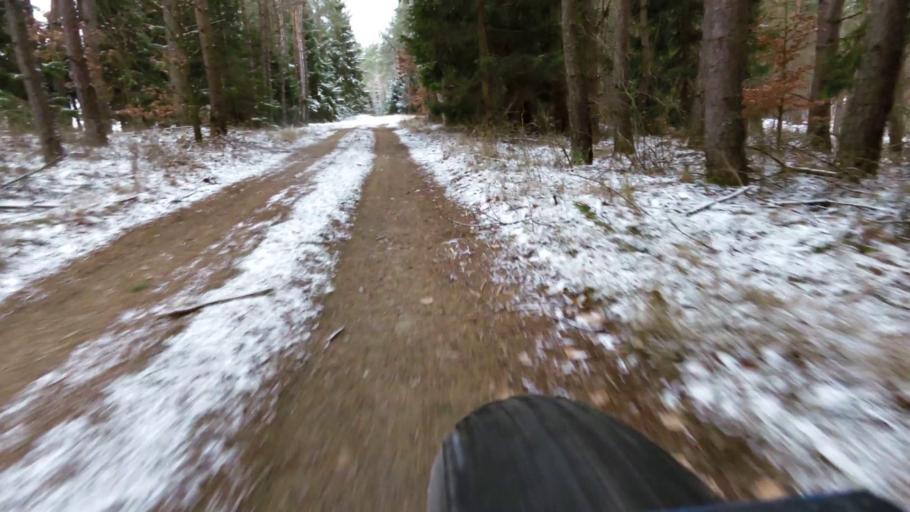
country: PL
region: West Pomeranian Voivodeship
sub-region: Powiat walecki
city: Miroslawiec
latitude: 53.3736
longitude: 16.1672
